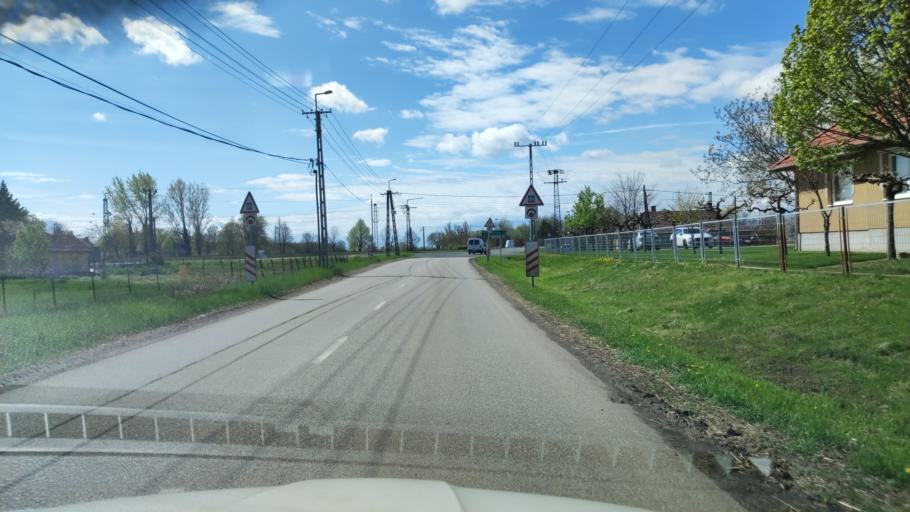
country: HU
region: Pest
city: Abony
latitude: 47.1737
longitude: 20.0048
